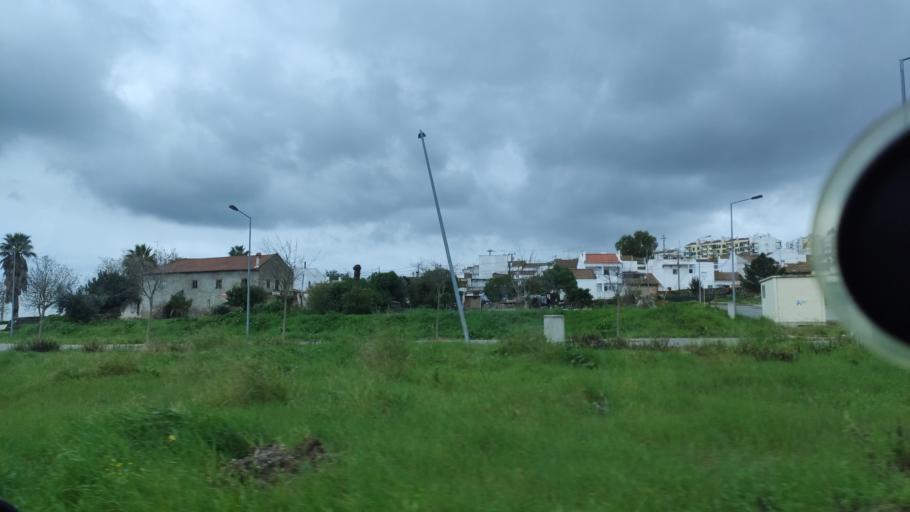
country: PT
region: Beja
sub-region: Beja
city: Beja
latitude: 38.0154
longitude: -7.8507
